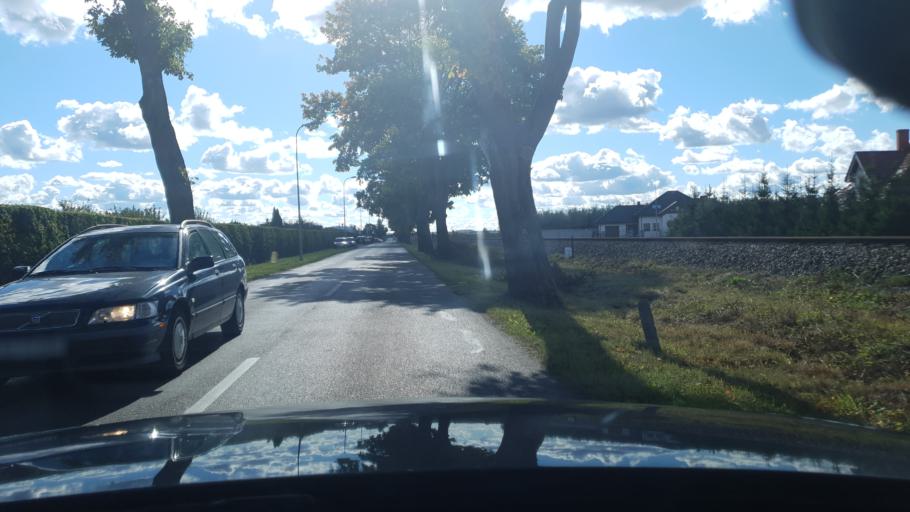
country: PL
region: Pomeranian Voivodeship
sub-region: Powiat pucki
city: Puck
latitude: 54.7057
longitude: 18.4115
